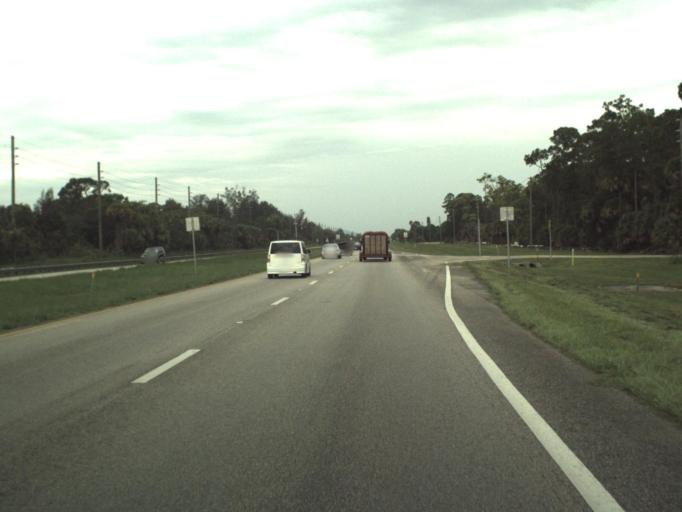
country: US
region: Florida
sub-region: Palm Beach County
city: Loxahatchee Groves
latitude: 26.6822
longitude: -80.2605
